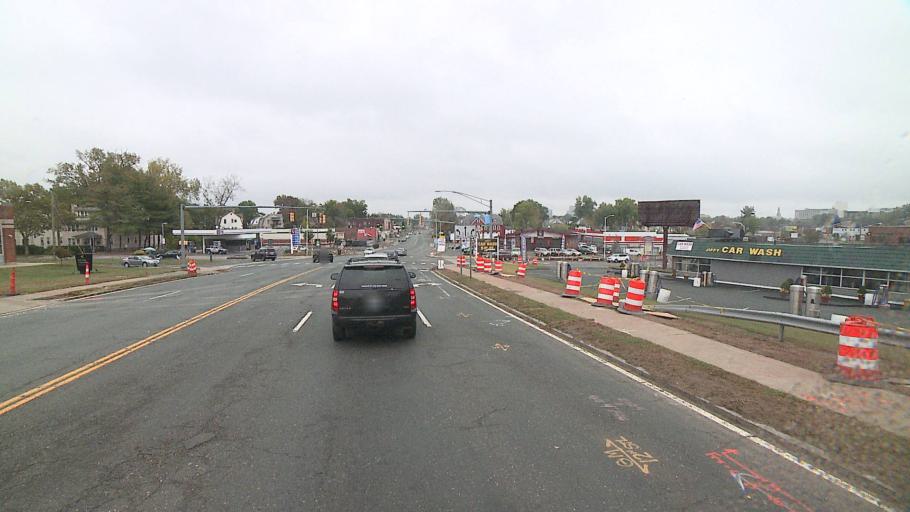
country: US
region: Connecticut
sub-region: Hartford County
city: Hartford
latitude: 41.7844
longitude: -72.7038
